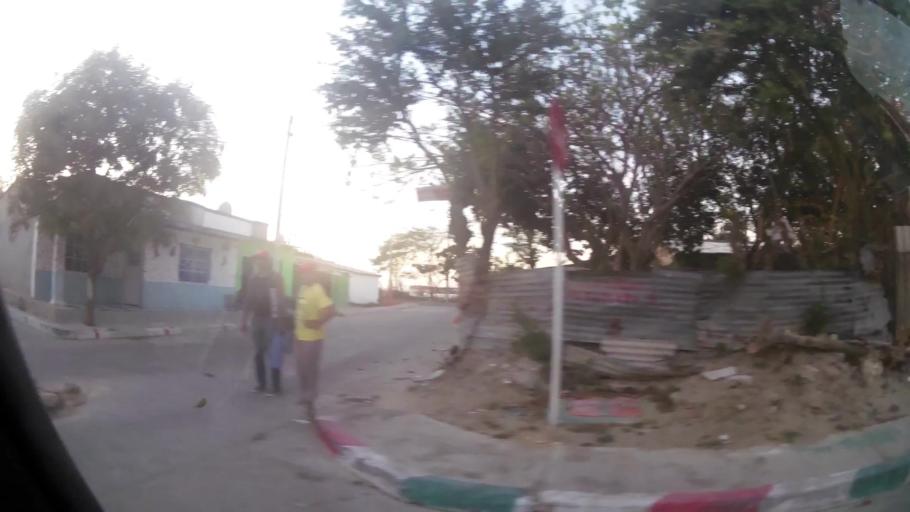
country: CO
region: Atlantico
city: Barranquilla
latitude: 10.9568
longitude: -74.8337
